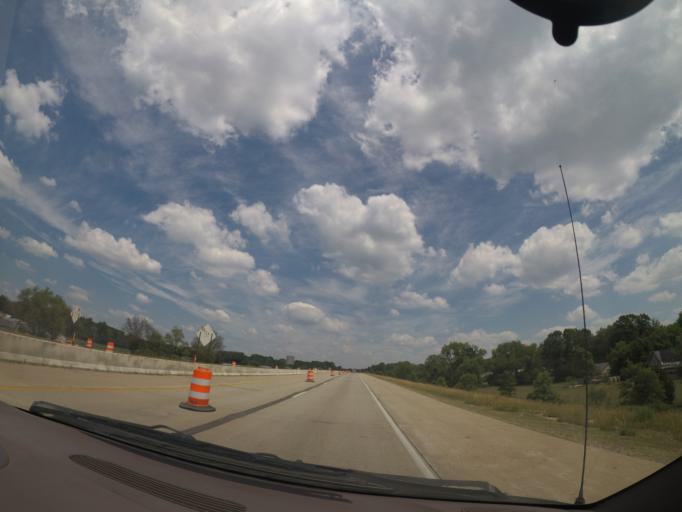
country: US
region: Indiana
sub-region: Elkhart County
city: Dunlap
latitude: 41.6570
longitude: -85.9257
